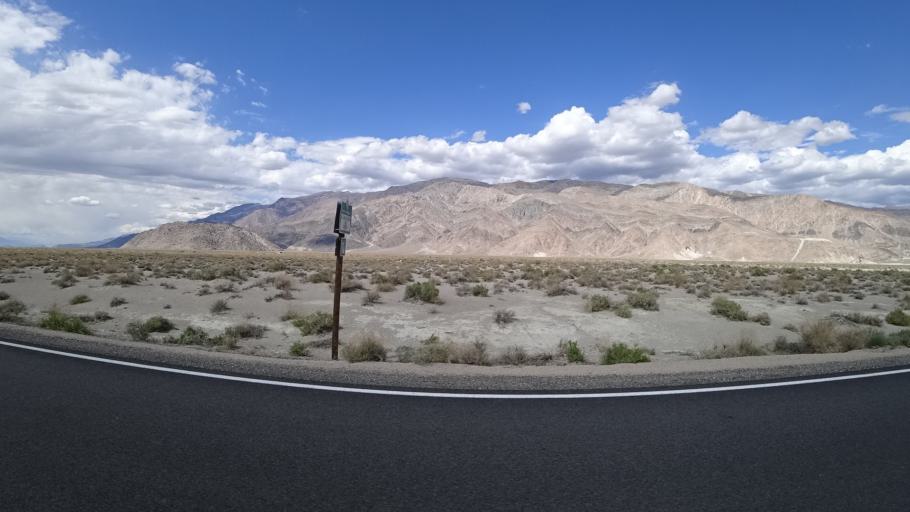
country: US
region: California
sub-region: Inyo County
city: Lone Pine
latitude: 36.5707
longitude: -117.9884
